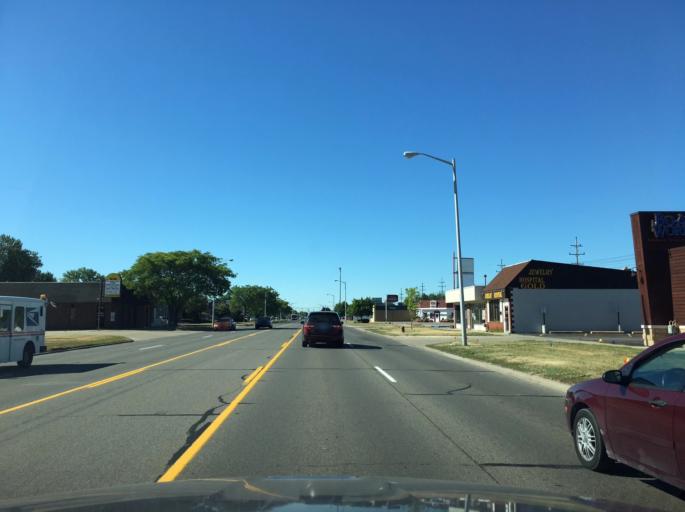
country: US
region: Michigan
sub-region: Macomb County
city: Saint Clair Shores
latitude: 42.5141
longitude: -82.8978
